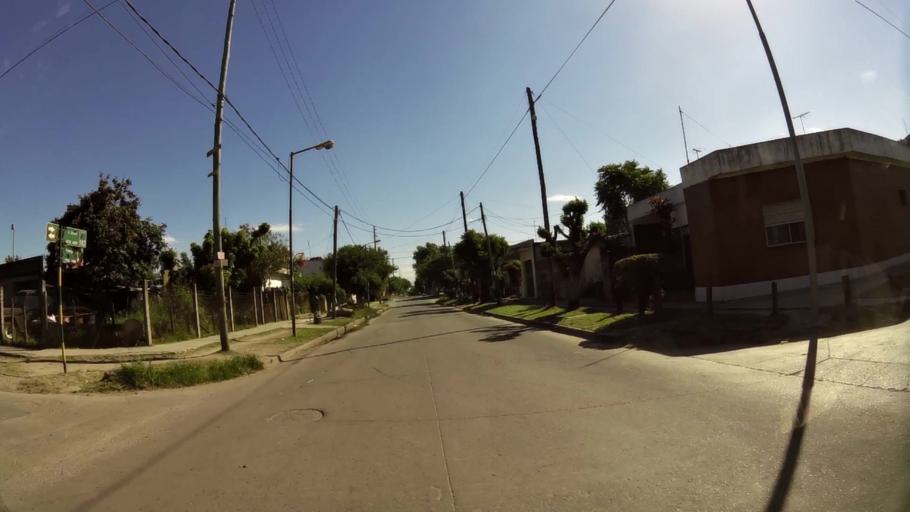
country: AR
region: Buenos Aires
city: Caseros
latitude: -34.5439
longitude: -58.5918
